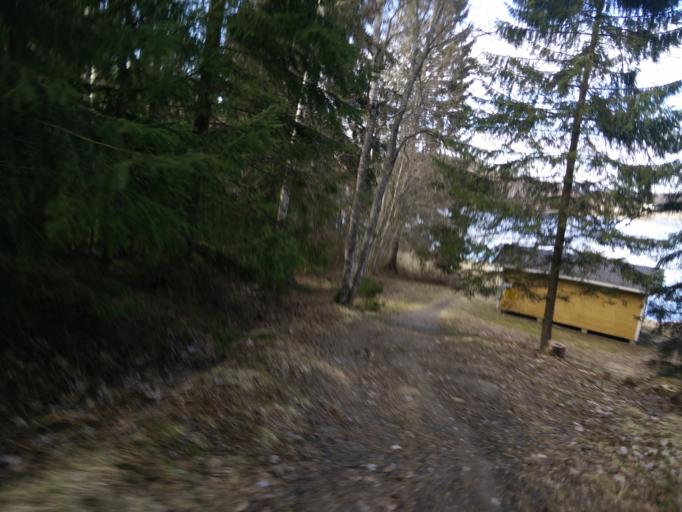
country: FI
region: Pirkanmaa
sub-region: Tampere
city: Orivesi
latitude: 61.6994
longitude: 24.3652
